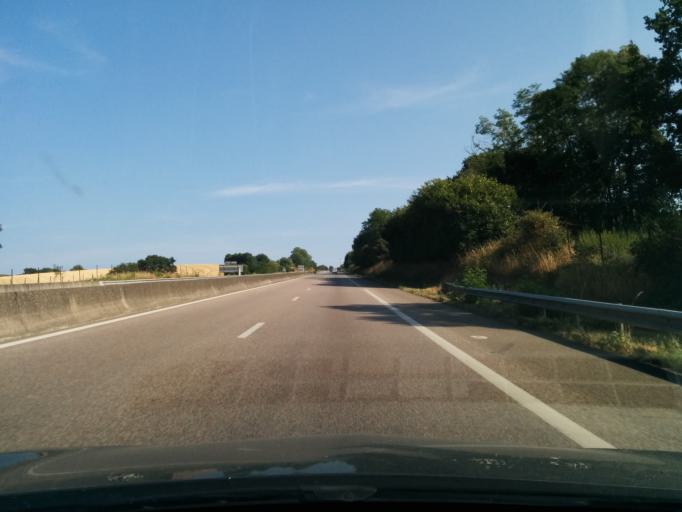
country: FR
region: Limousin
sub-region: Departement de la Haute-Vienne
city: Pierre-Buffiere
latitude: 45.7217
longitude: 1.3501
